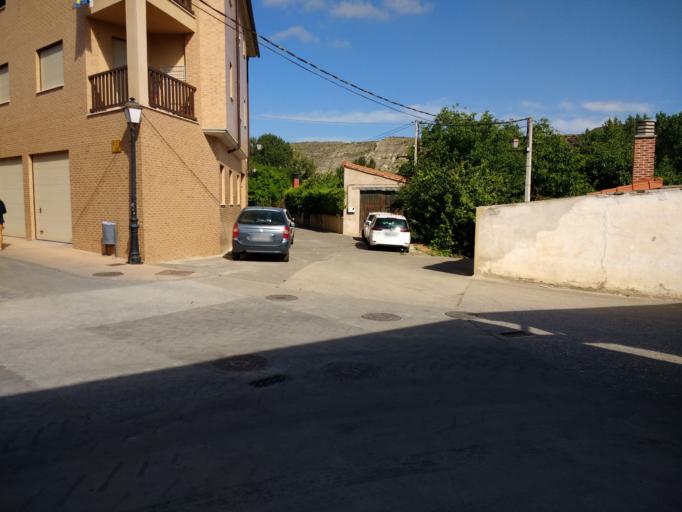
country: ES
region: La Rioja
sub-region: Provincia de La Rioja
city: Leiva
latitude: 42.5022
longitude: -3.0491
